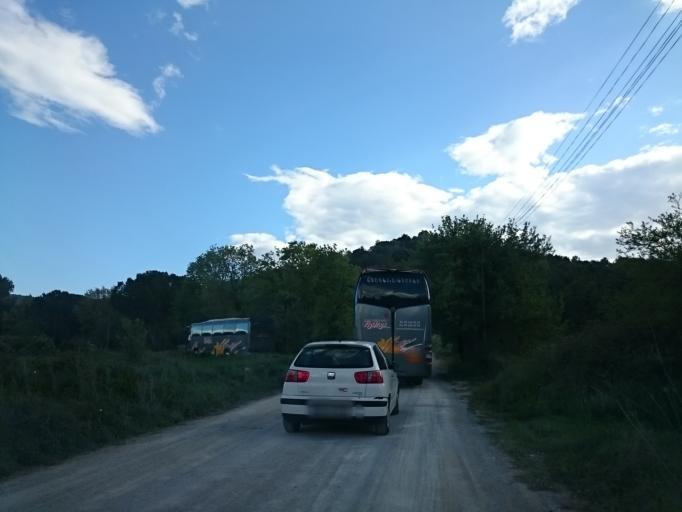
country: ES
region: Catalonia
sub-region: Provincia de Barcelona
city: Begues
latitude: 41.3247
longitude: 1.9252
